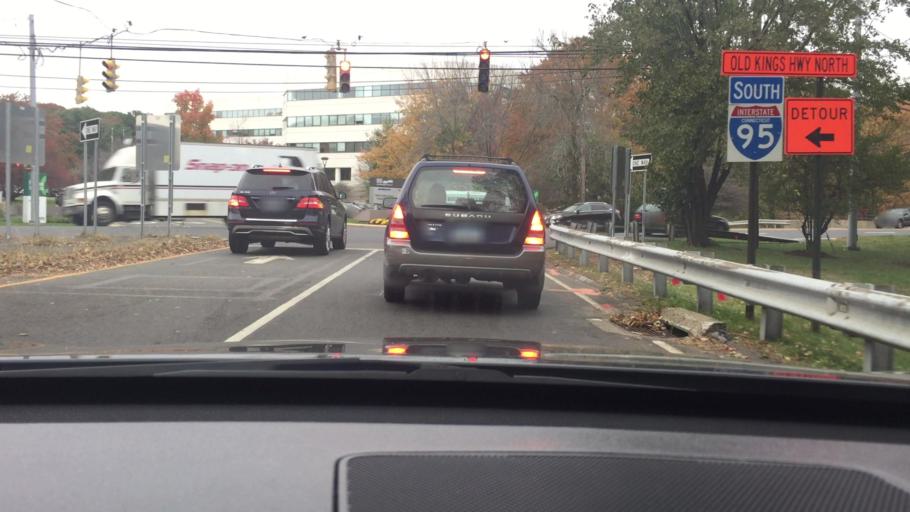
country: US
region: Connecticut
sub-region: Fairfield County
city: Darien
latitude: 41.0913
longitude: -73.4539
